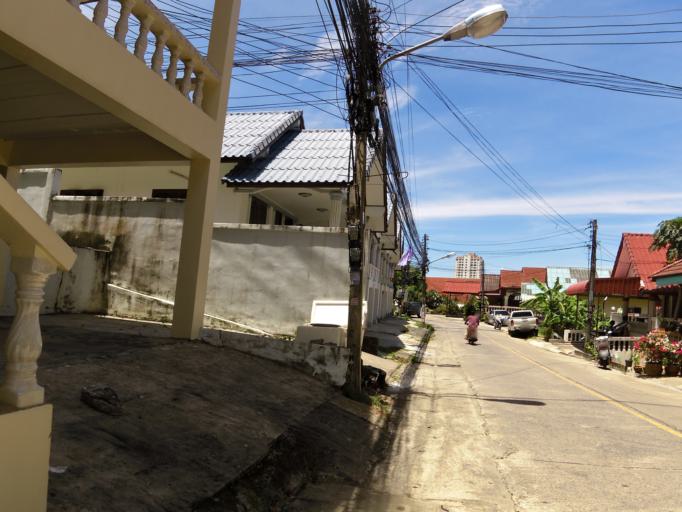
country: TH
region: Phuket
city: Ban Karon
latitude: 7.8488
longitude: 98.3007
